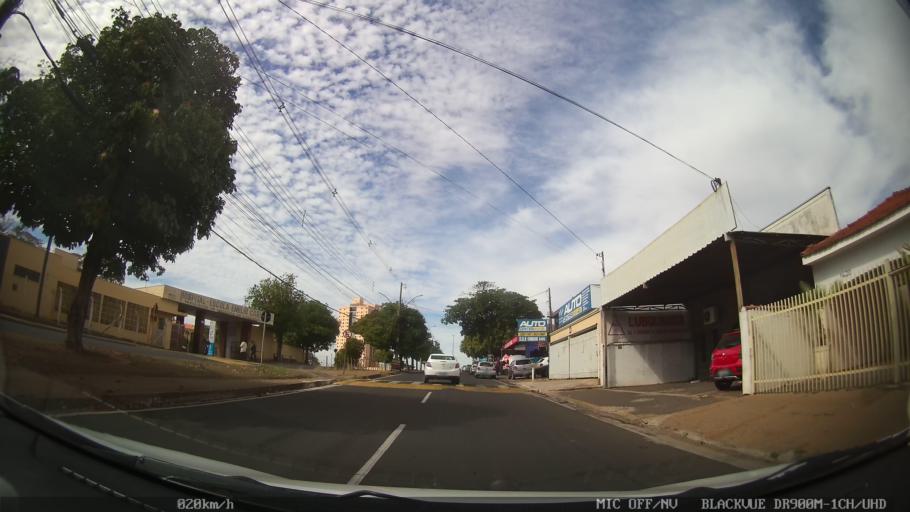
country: BR
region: Sao Paulo
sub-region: Catanduva
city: Catanduva
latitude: -21.1501
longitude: -48.9602
